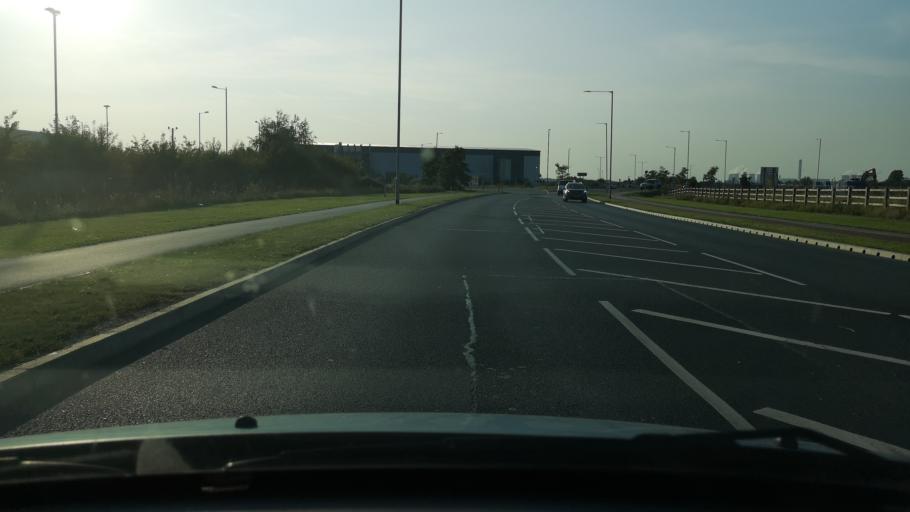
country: GB
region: England
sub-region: East Riding of Yorkshire
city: Airmyn
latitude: 53.6997
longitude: -0.9027
